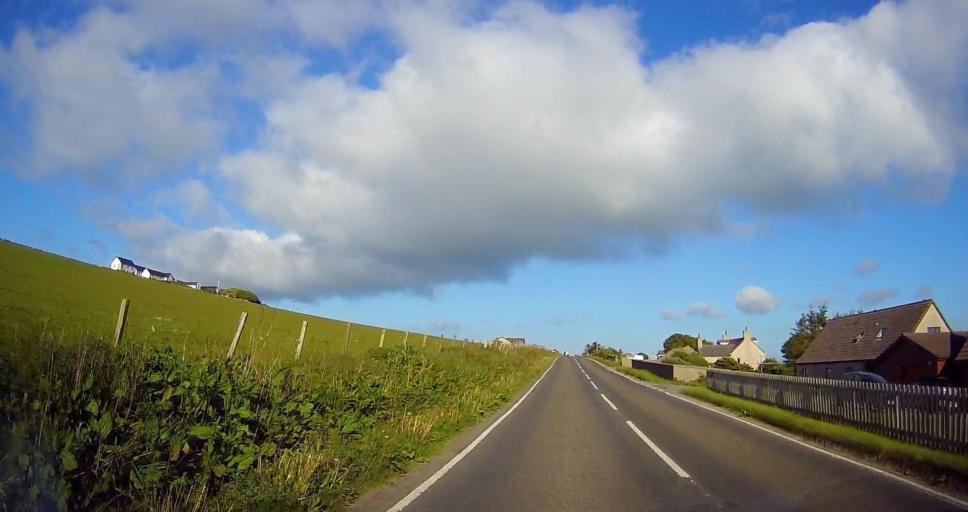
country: GB
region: Scotland
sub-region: Orkney Islands
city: Orkney
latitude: 58.9787
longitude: -3.0179
